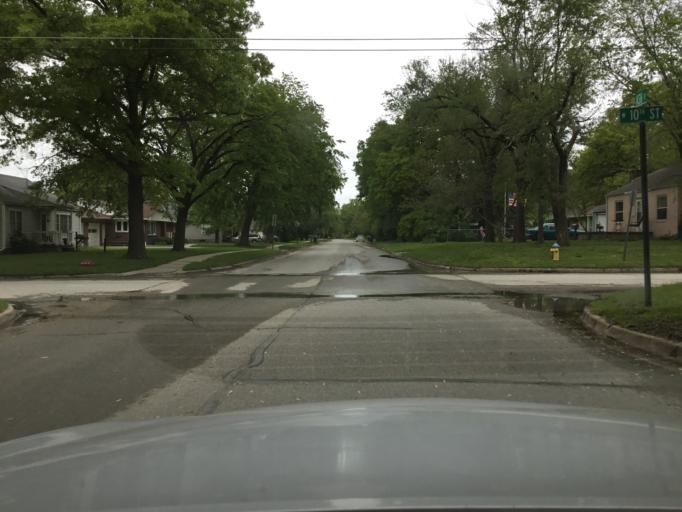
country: US
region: Kansas
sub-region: Franklin County
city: Ottawa
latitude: 38.6028
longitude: -95.2770
